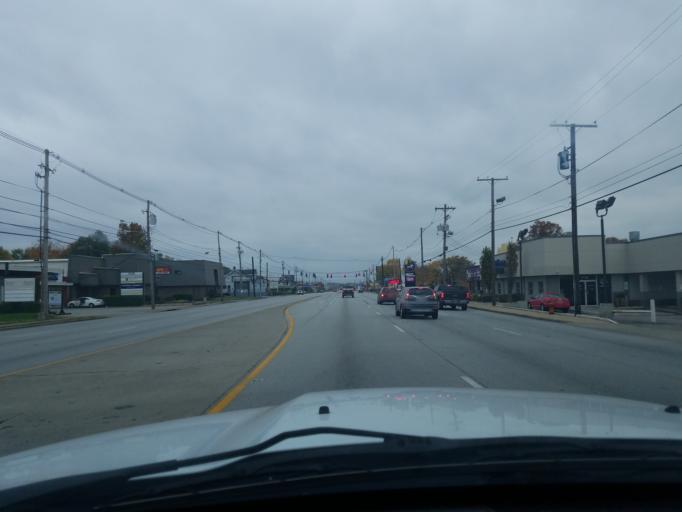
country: US
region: Kentucky
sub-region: Jefferson County
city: Saint Dennis
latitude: 38.1661
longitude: -85.8299
